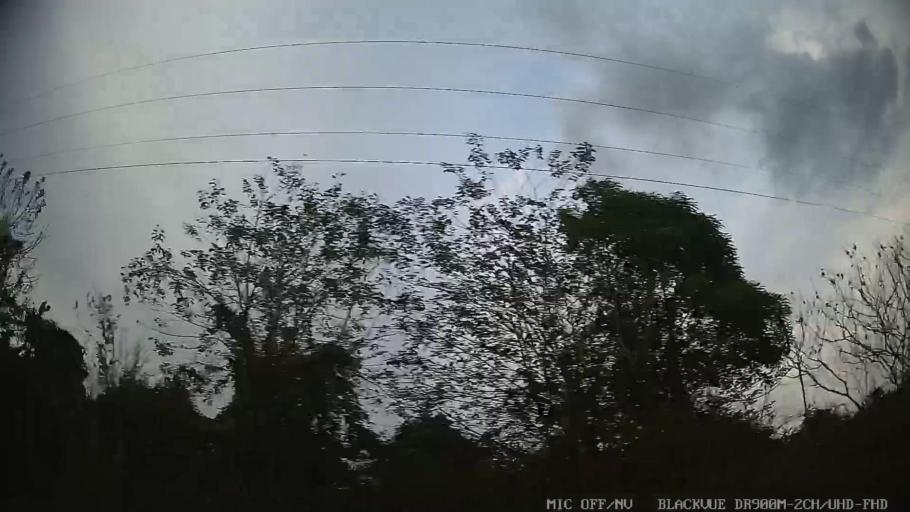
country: BR
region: Sao Paulo
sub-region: Itatiba
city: Itatiba
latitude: -23.0075
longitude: -46.8999
